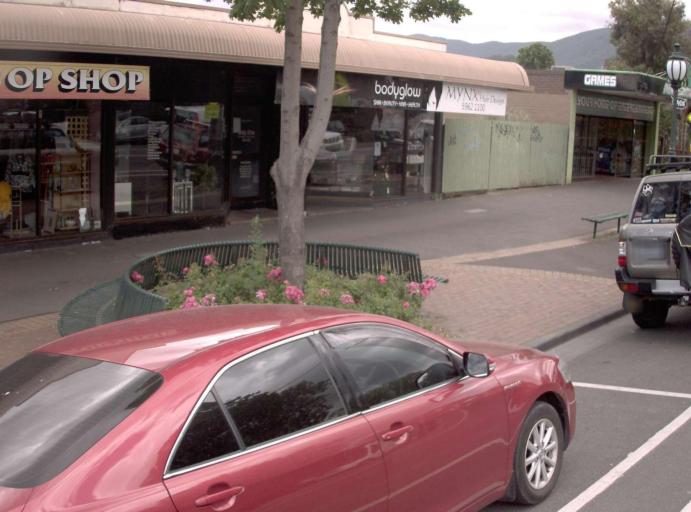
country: AU
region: Victoria
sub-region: Yarra Ranges
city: Healesville
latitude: -37.6511
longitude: 145.5224
